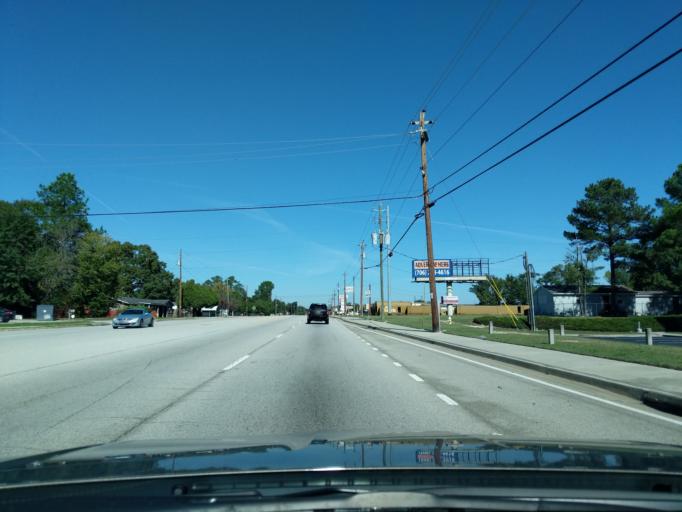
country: US
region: Georgia
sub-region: Richmond County
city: Augusta
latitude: 33.4054
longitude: -82.0061
